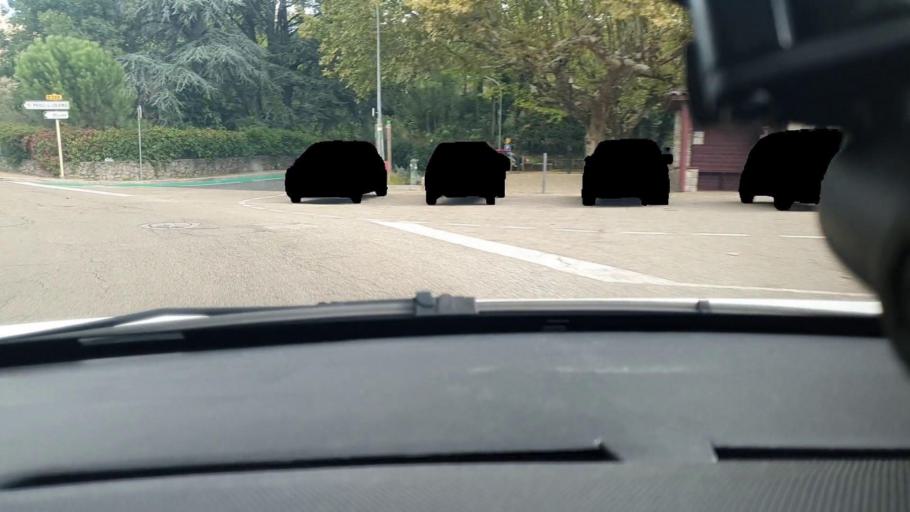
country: FR
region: Languedoc-Roussillon
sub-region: Departement du Gard
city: Besseges
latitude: 44.3077
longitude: 4.1292
